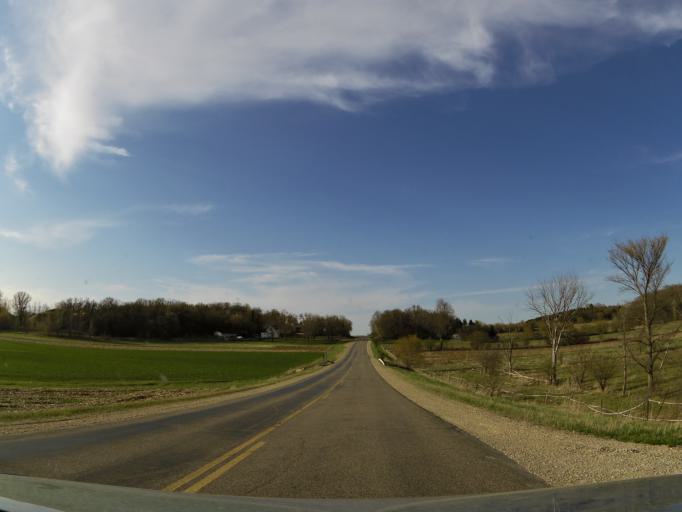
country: US
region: Wisconsin
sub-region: Pierce County
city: River Falls
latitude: 44.7525
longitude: -92.6396
